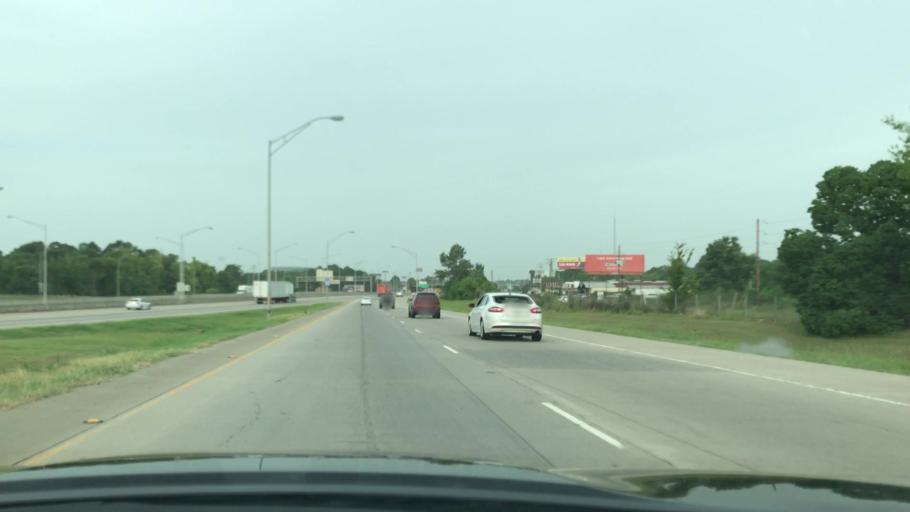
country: US
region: Louisiana
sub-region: Caddo Parish
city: Shreveport
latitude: 32.4552
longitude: -93.8494
